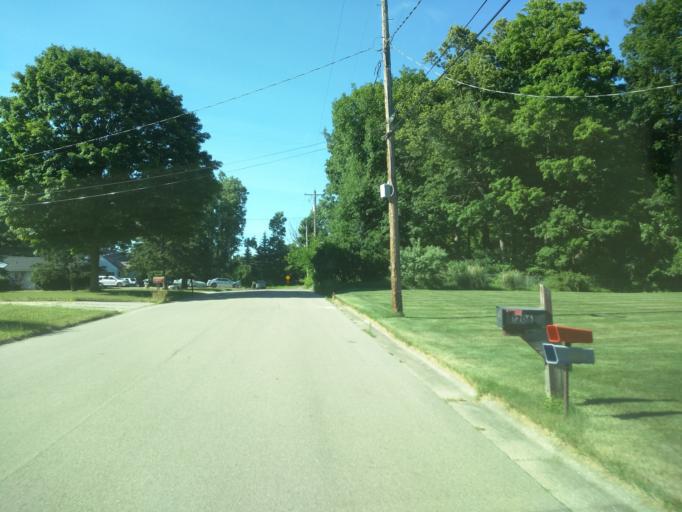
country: US
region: Michigan
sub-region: Eaton County
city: Waverly
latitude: 42.7473
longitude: -84.6360
